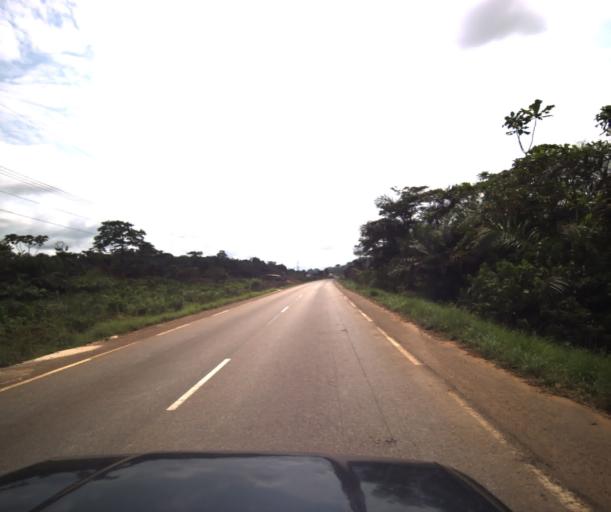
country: CM
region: Centre
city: Eseka
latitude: 3.8557
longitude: 10.5309
